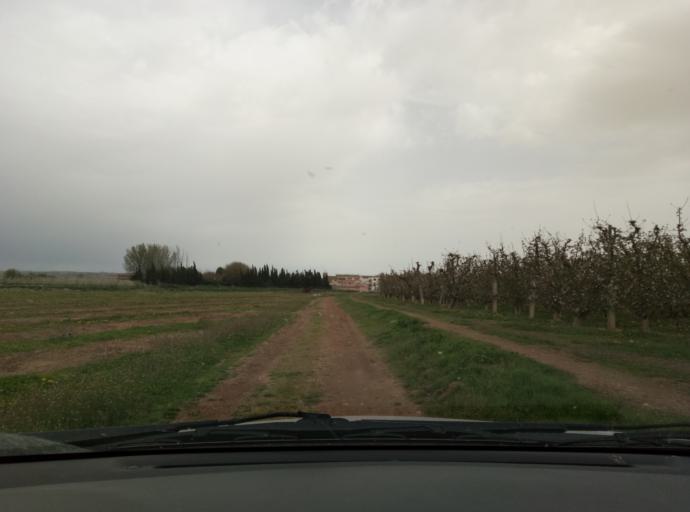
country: ES
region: Catalonia
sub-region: Provincia de Lleida
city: La Fuliola
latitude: 41.7044
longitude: 1.0298
